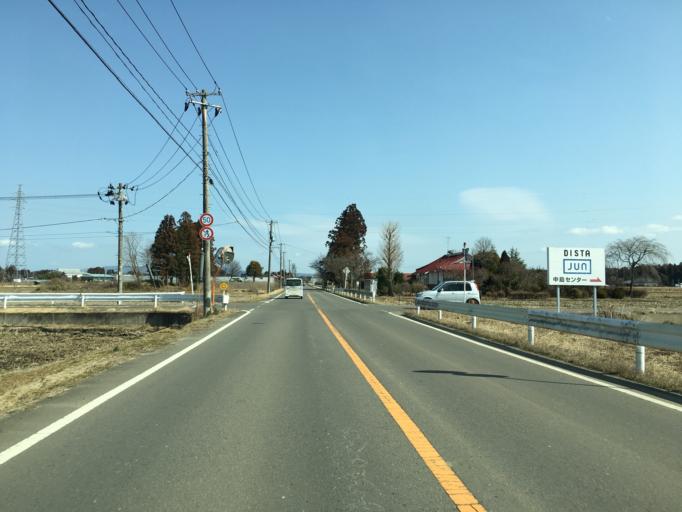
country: JP
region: Fukushima
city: Ishikawa
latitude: 37.1388
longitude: 140.3362
